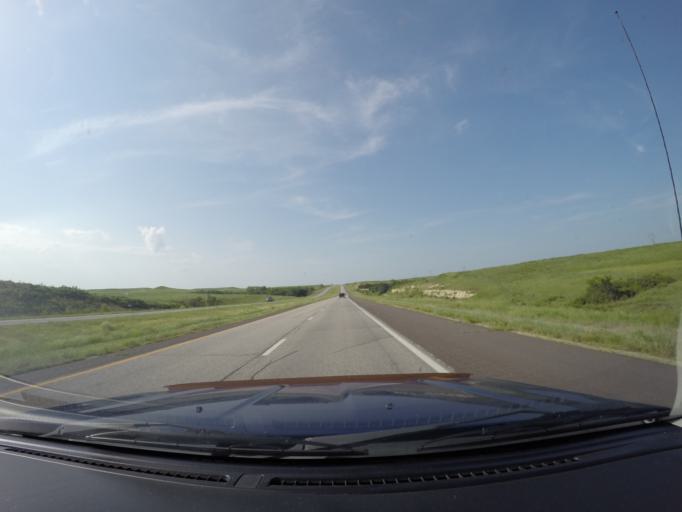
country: US
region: Kansas
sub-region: Riley County
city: Manhattan
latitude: 39.0804
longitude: -96.5382
